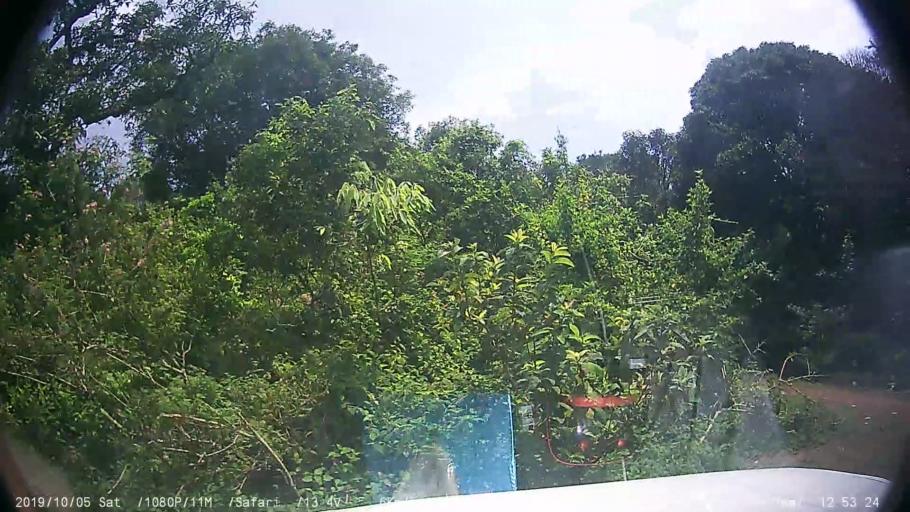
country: IN
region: Kerala
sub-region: Kottayam
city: Erattupetta
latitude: 9.5726
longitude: 76.9712
